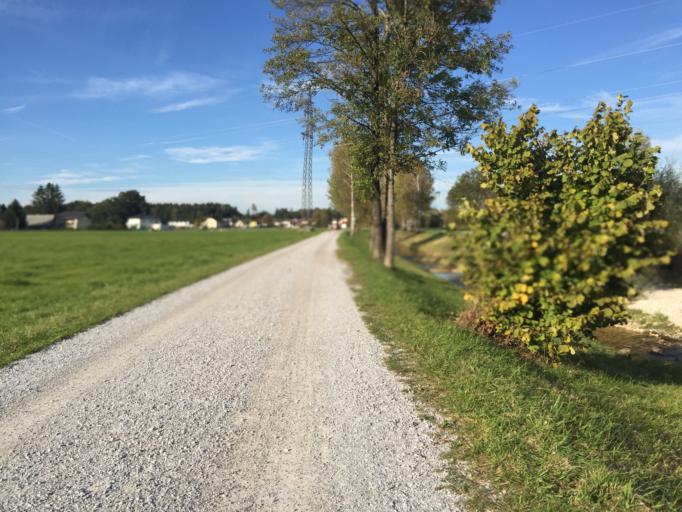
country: AT
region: Salzburg
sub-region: Politischer Bezirk Salzburg-Umgebung
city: Grodig
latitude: 47.7685
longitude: 13.0006
